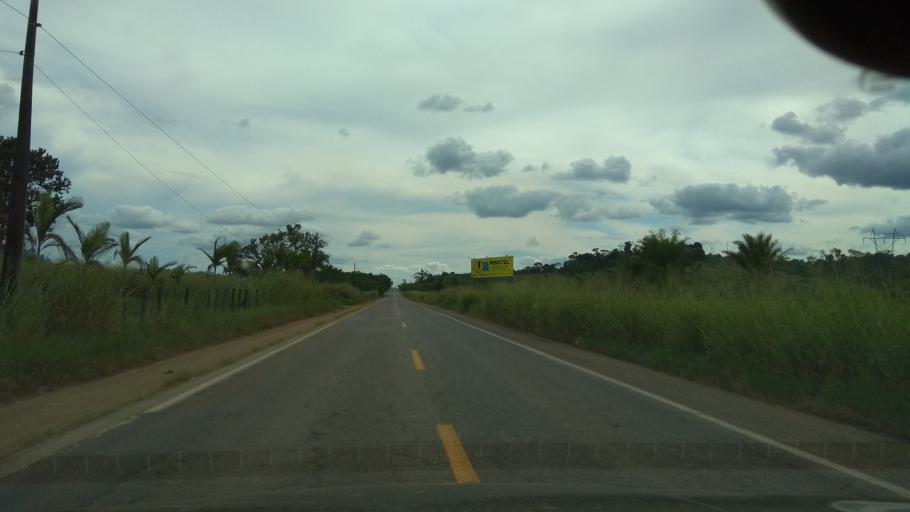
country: BR
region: Bahia
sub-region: Ipiau
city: Ipiau
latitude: -14.1468
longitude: -39.7066
